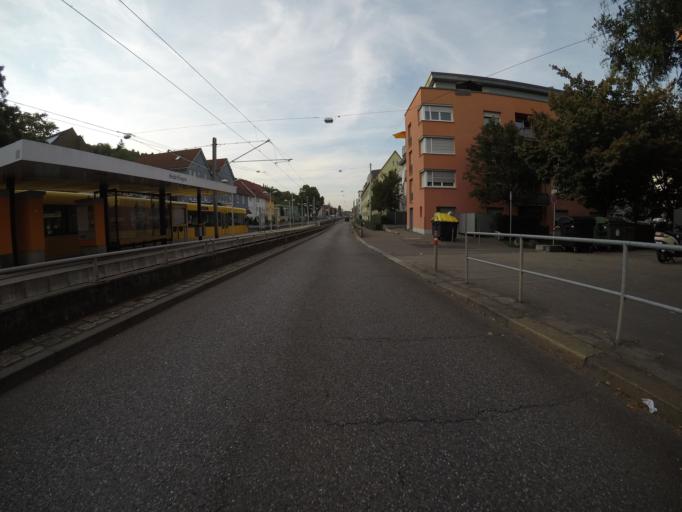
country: DE
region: Baden-Wuerttemberg
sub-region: Regierungsbezirk Stuttgart
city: Ostfildern
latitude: 48.7599
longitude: 9.2545
